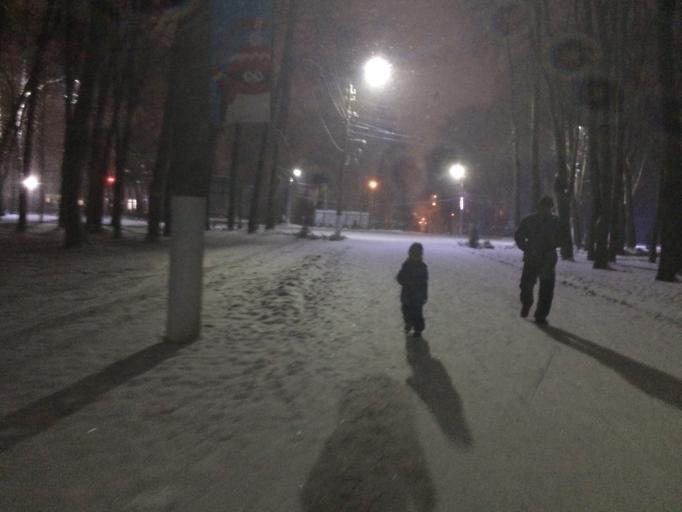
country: RU
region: Tula
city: Tula
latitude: 54.1784
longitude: 37.5934
